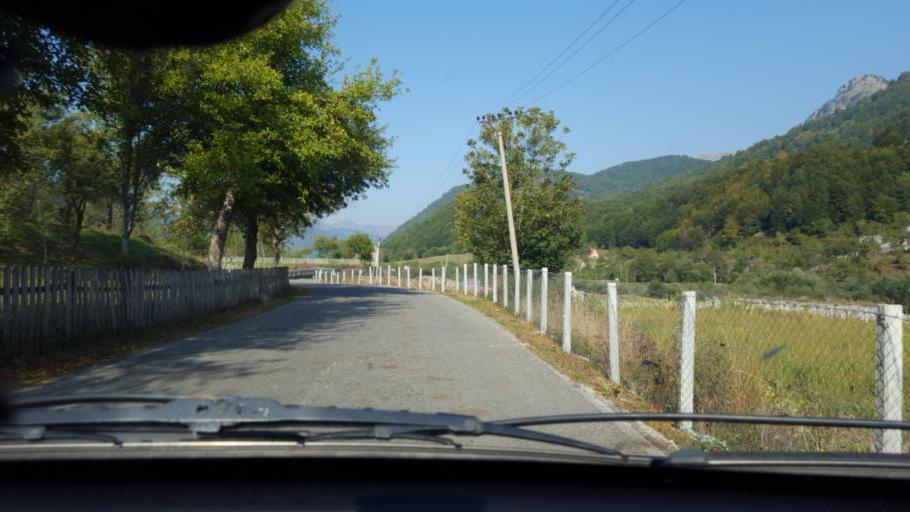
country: ME
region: Andrijevica
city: Andrijevica
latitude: 42.5874
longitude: 19.7160
